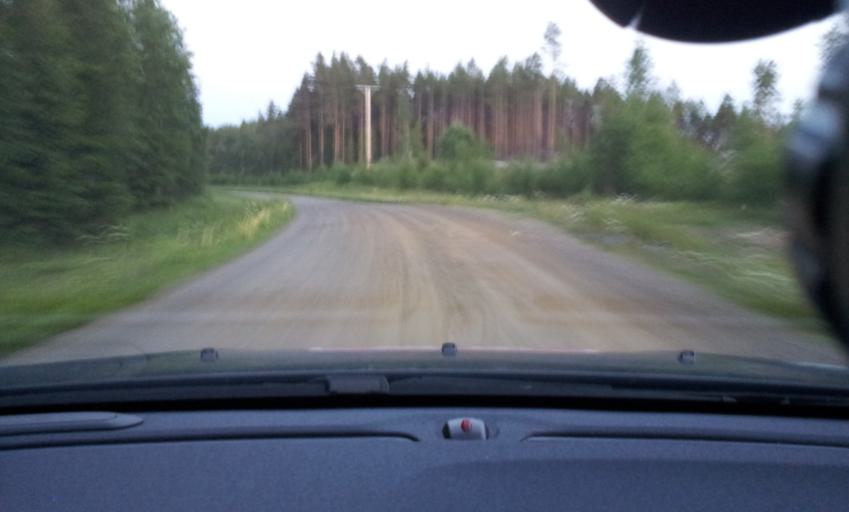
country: SE
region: Vaesternorrland
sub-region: Ange Kommun
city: Fransta
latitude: 62.8212
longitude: 16.0067
